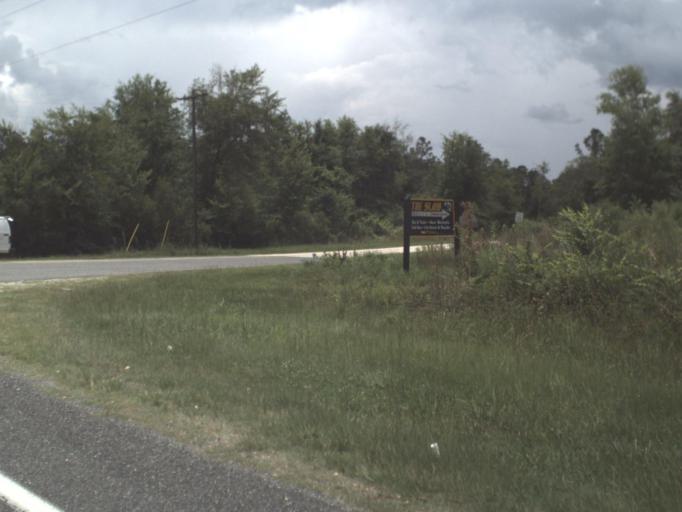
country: US
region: Florida
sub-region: Bradford County
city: Starke
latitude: 29.9624
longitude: -82.1754
